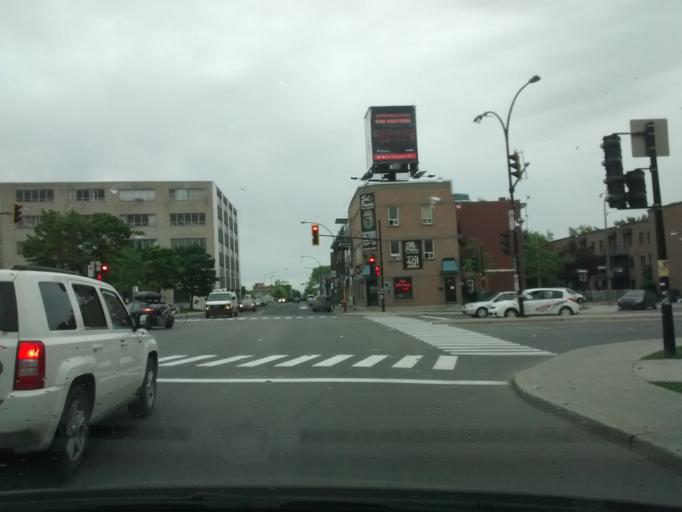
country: CA
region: Quebec
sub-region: Montreal
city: Montreal
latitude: 45.5432
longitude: -73.5786
